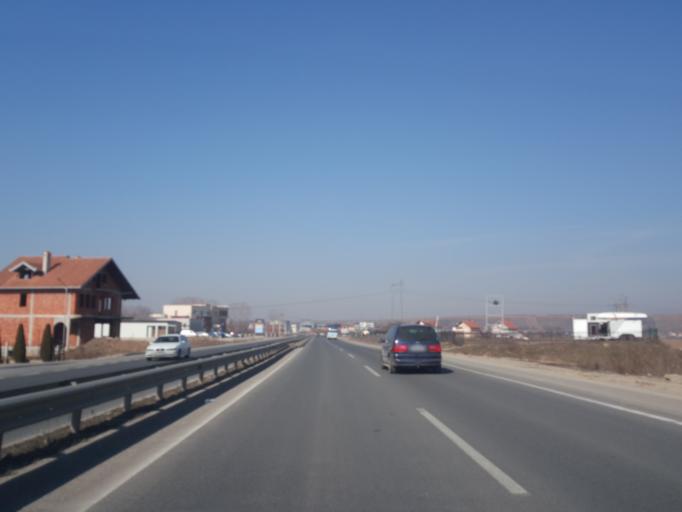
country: XK
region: Pristina
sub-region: Komuna e Obiliqit
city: Obiliq
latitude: 42.7298
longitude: 21.0755
